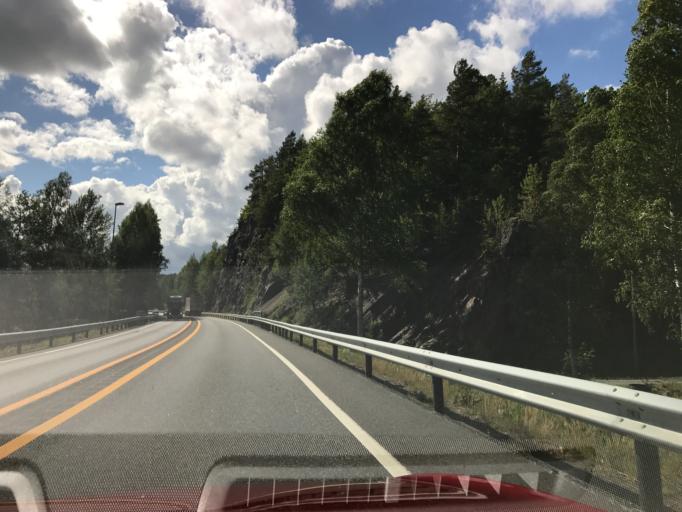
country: NO
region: Telemark
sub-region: Kragero
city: Kragero
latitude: 58.9610
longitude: 9.4458
